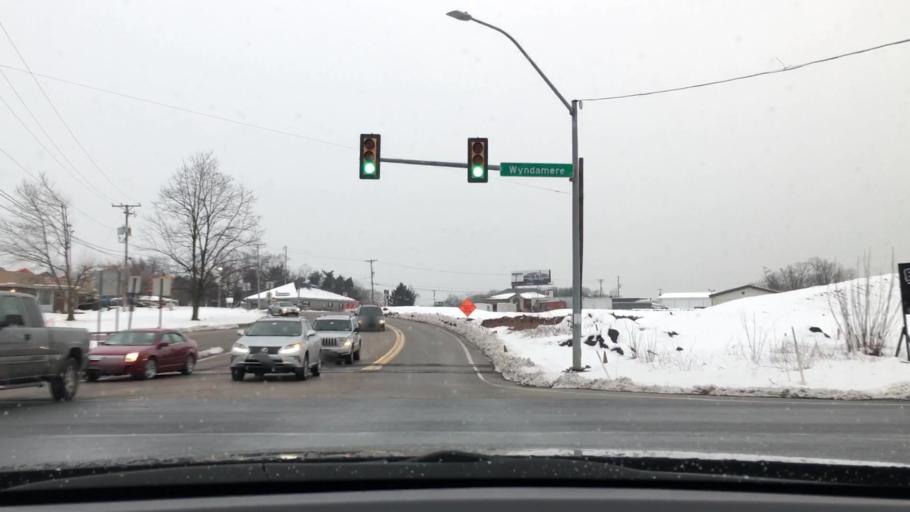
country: US
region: Pennsylvania
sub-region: York County
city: Valley Green
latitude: 40.1654
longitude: -76.8306
